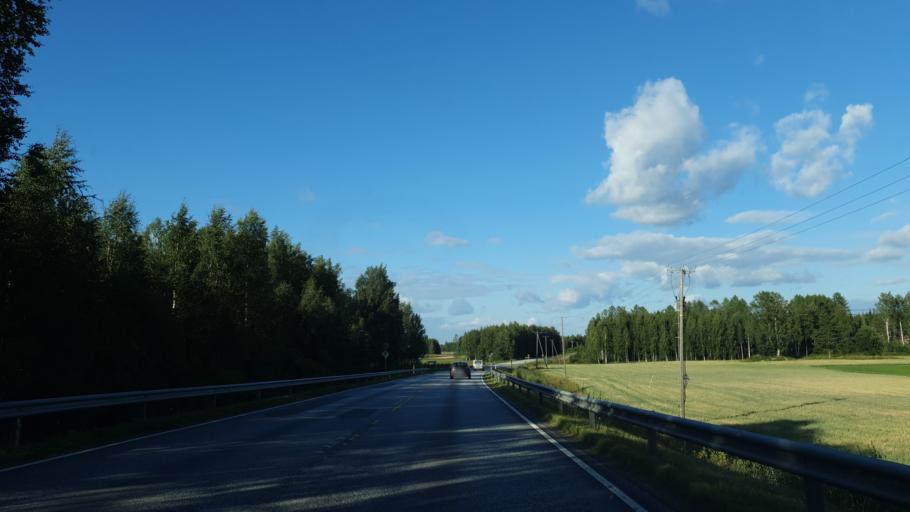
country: FI
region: North Karelia
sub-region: Joensuu
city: Outokumpu
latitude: 62.5677
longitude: 29.1511
